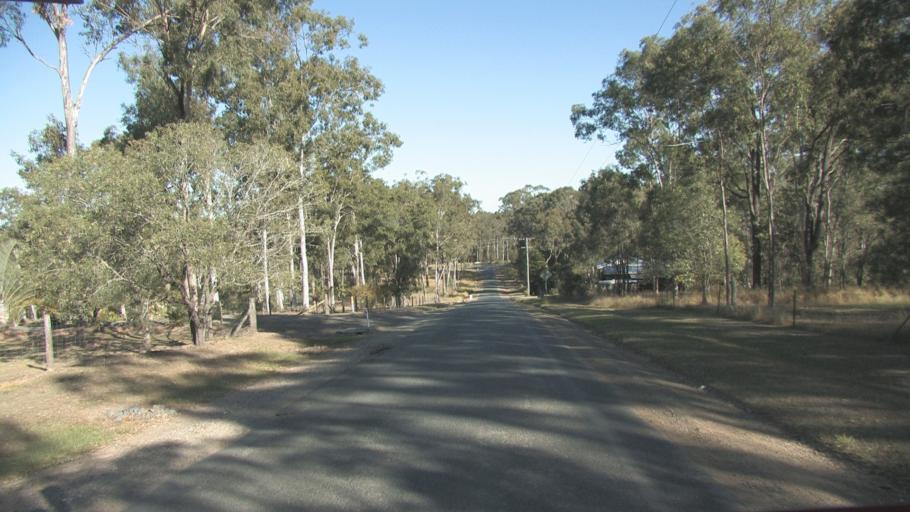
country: AU
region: Queensland
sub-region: Logan
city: North Maclean
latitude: -27.8086
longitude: 153.0336
